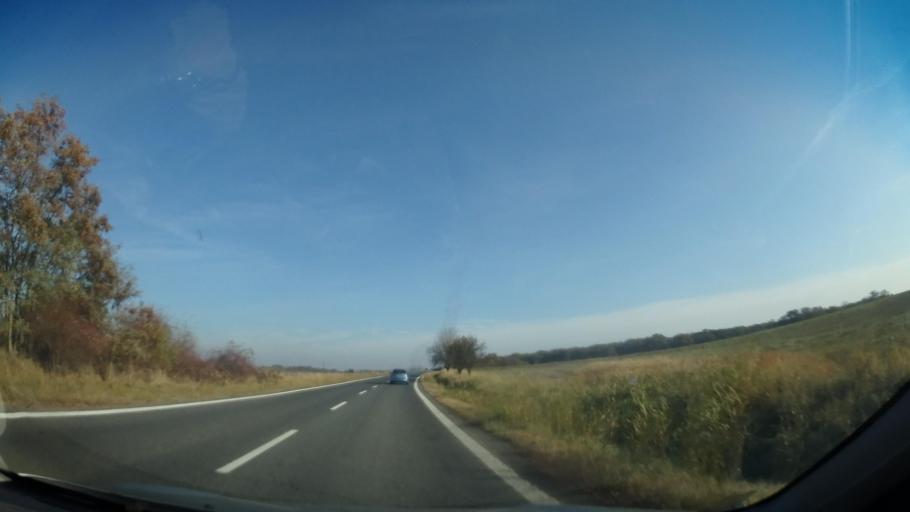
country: CZ
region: Praha
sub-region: Praha 20
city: Horni Pocernice
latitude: 50.0628
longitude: 14.6198
